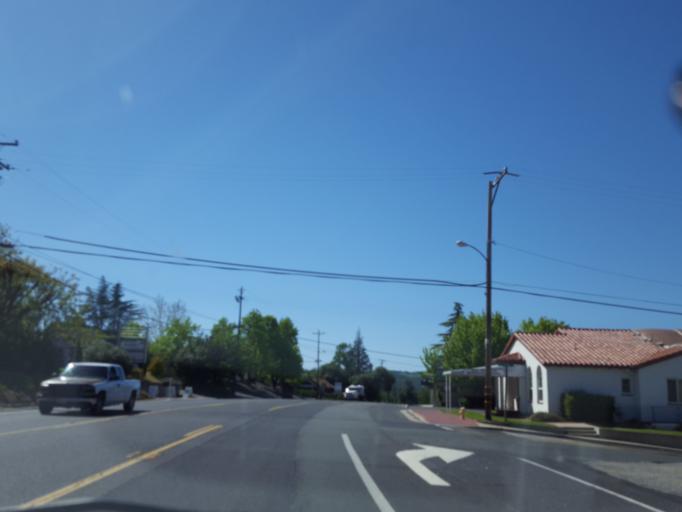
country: US
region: California
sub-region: Calaveras County
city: San Andreas
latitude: 38.1975
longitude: -120.6853
